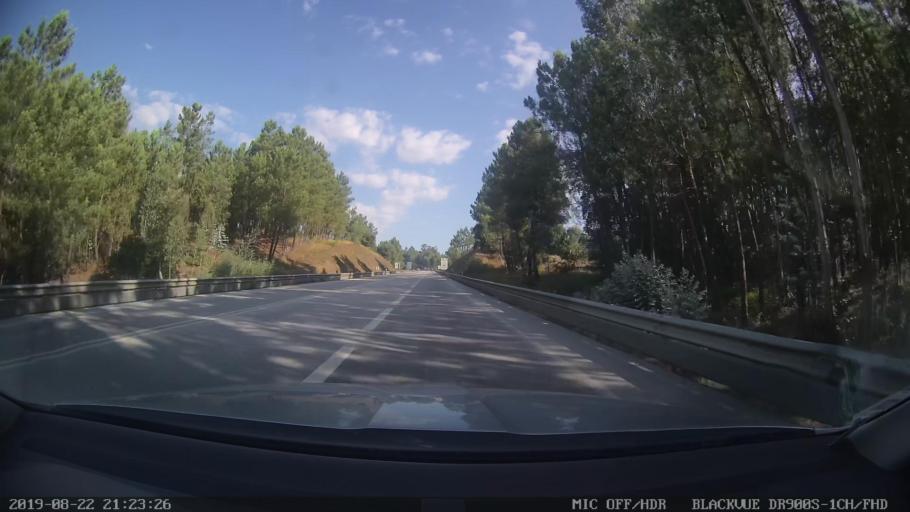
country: PT
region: Castelo Branco
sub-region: Serta
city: Serta
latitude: 39.8308
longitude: -8.1094
